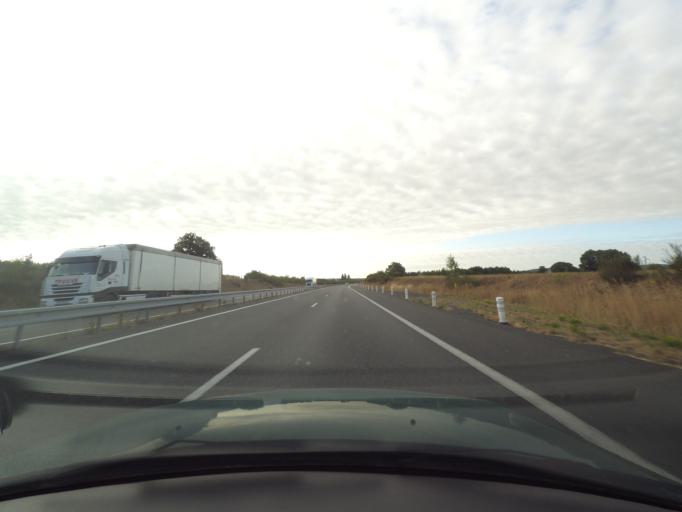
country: FR
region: Pays de la Loire
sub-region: Departement de Maine-et-Loire
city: La Tessoualle
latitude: 46.9717
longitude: -0.8066
